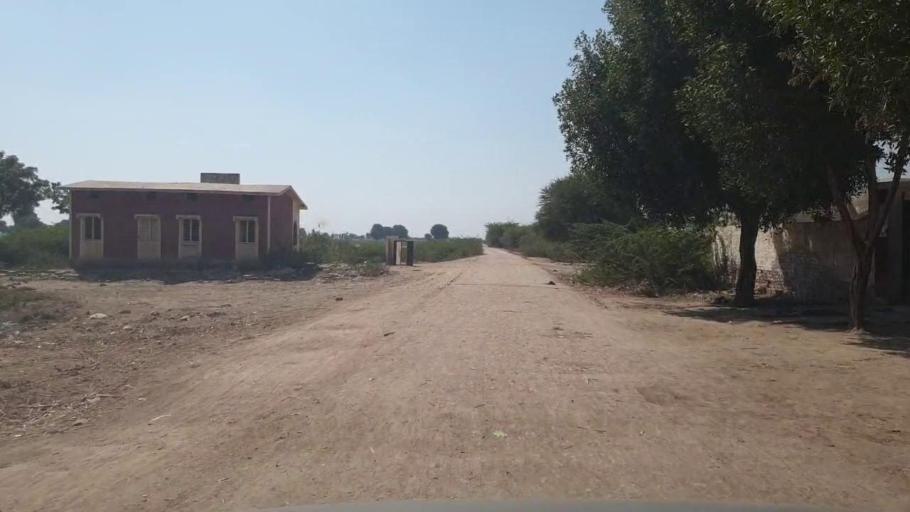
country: PK
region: Sindh
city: Digri
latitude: 25.2407
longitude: 69.2264
